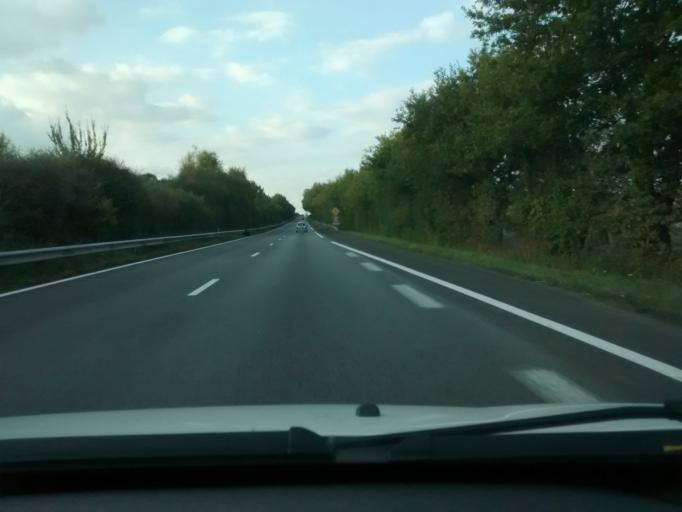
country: FR
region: Pays de la Loire
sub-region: Departement de la Loire-Atlantique
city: Jans
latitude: 47.6302
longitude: -1.6466
